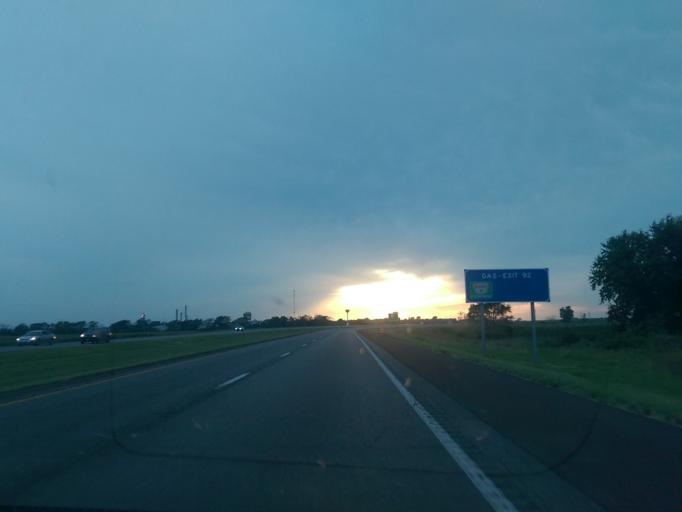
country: US
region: Missouri
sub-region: Holt County
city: Mound City
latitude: 40.1887
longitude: -95.3514
